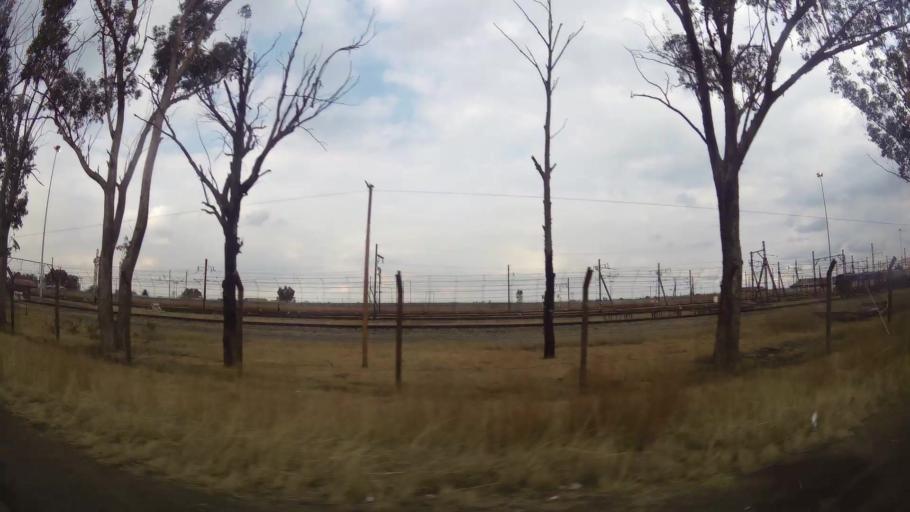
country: ZA
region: Orange Free State
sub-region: Fezile Dabi District Municipality
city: Sasolburg
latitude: -26.8472
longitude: 27.8696
